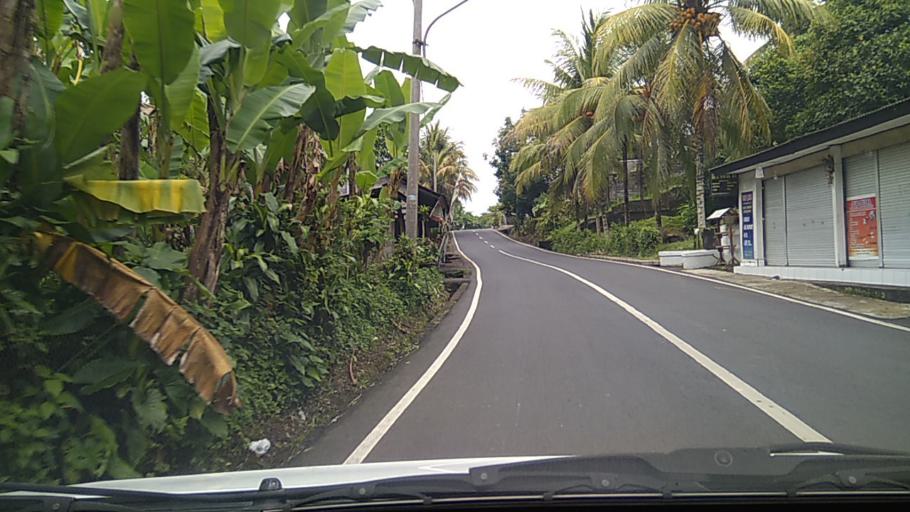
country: ID
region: Bali
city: Brahmana
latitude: -8.4731
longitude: 115.1929
